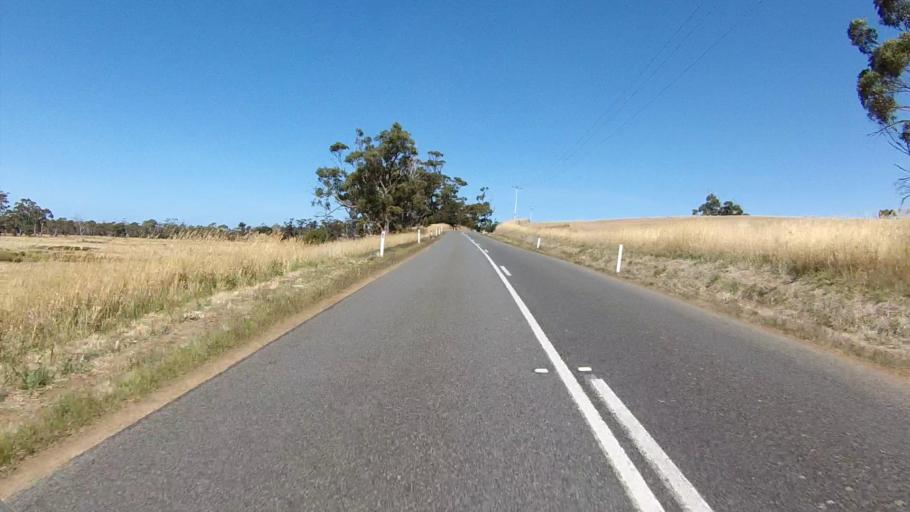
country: AU
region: Tasmania
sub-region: Sorell
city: Sorell
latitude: -42.2656
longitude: 148.0027
